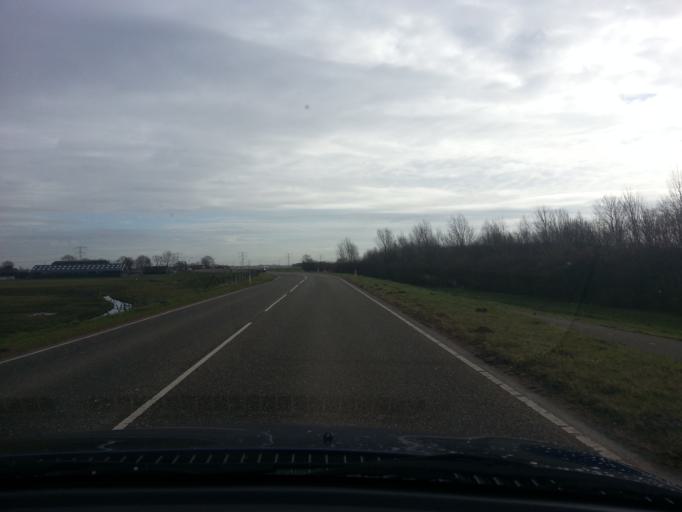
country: NL
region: South Holland
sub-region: Gemeente Spijkenisse
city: Spijkenisse
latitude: 51.8269
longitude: 4.2743
